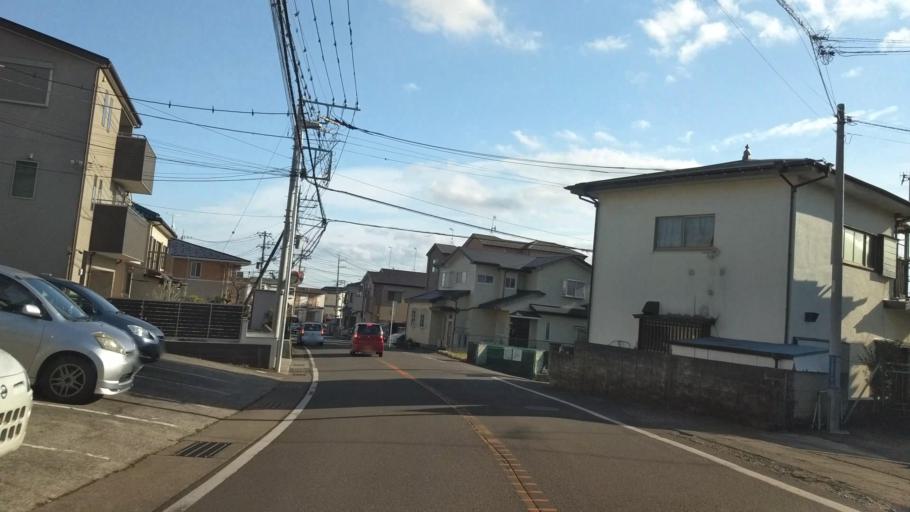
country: JP
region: Kanagawa
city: Isehara
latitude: 35.3768
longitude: 139.2820
